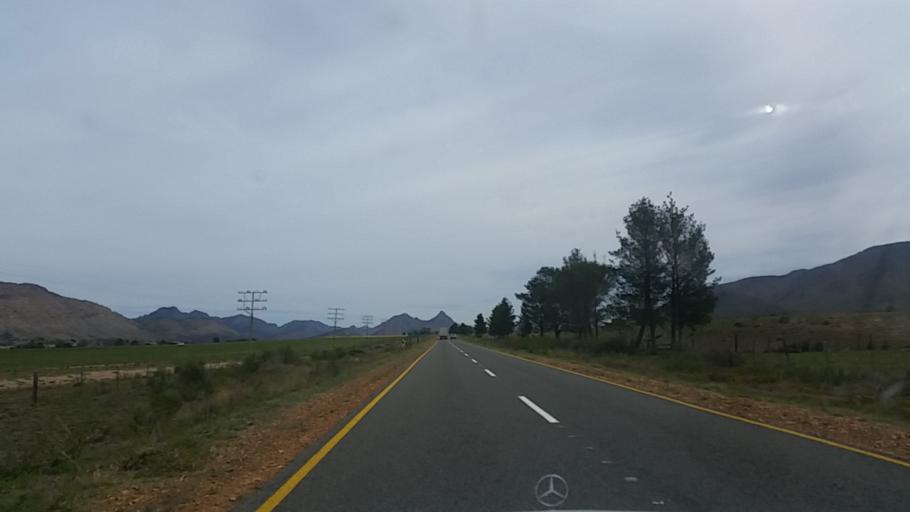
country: ZA
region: Western Cape
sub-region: Eden District Municipality
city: George
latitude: -33.8147
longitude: 22.5215
